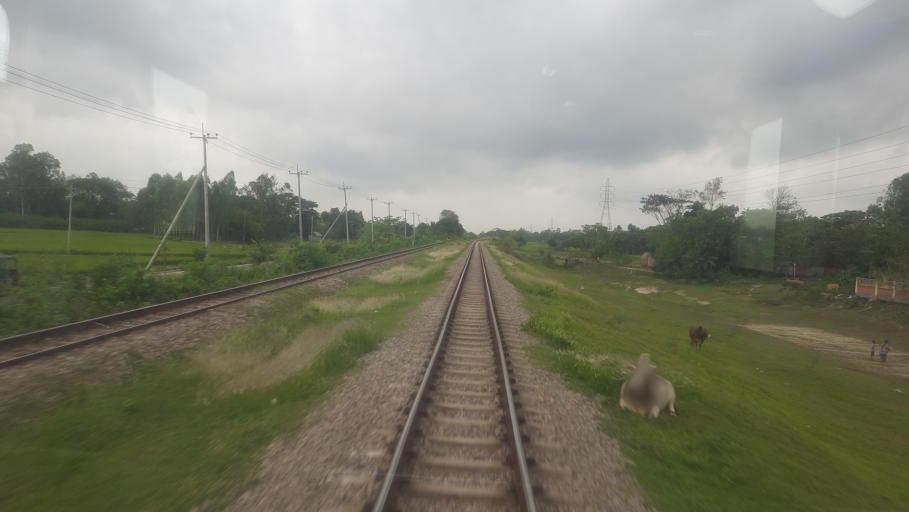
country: BD
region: Dhaka
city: Narsingdi
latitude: 23.9825
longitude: 90.8466
